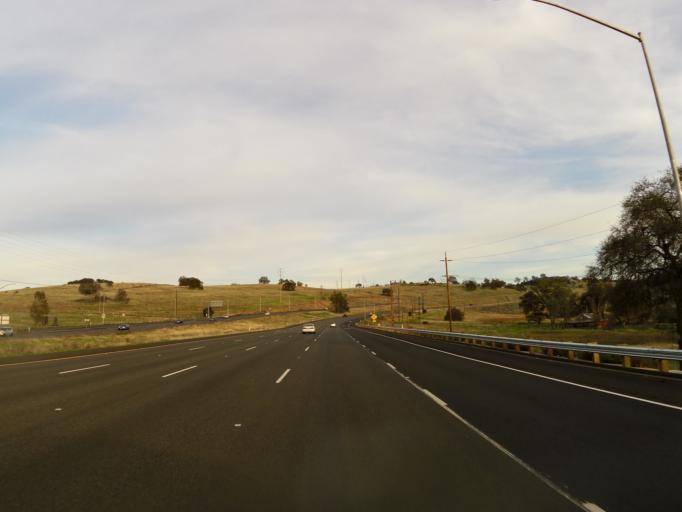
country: US
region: California
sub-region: El Dorado County
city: El Dorado Hills
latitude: 38.6581
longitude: -121.0520
